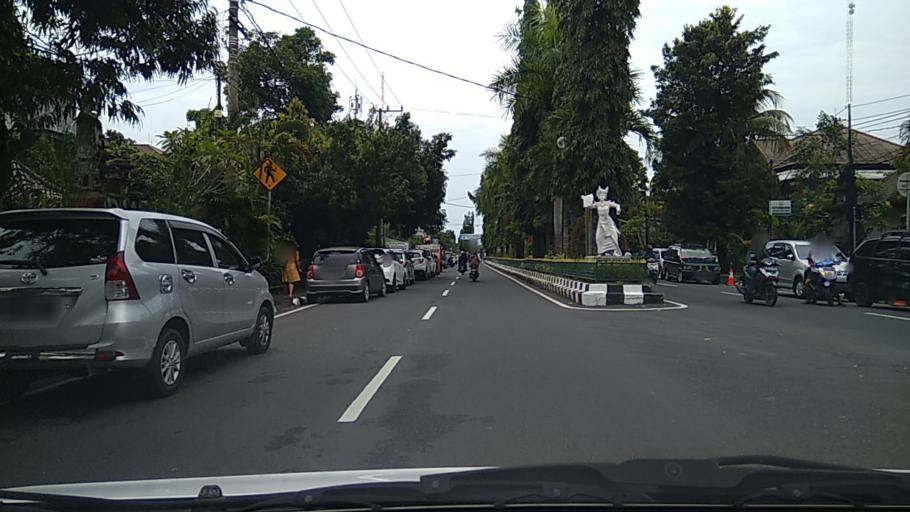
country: ID
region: Bali
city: Banjar Kelodan
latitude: -8.5386
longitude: 115.3227
